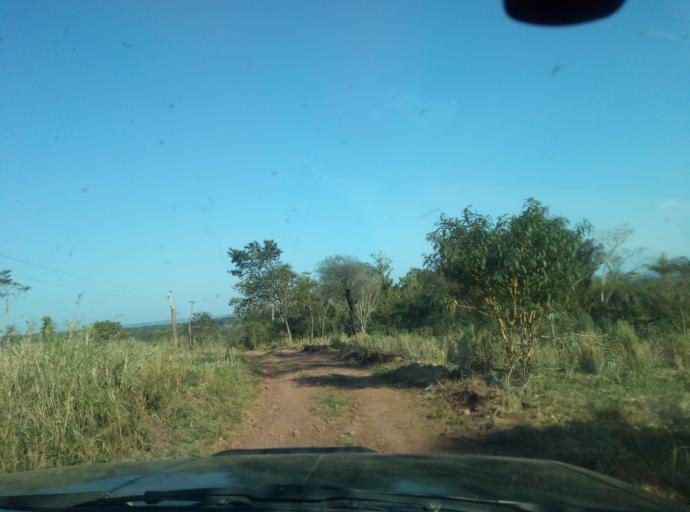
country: PY
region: Caaguazu
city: San Joaquin
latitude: -25.1685
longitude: -56.1151
